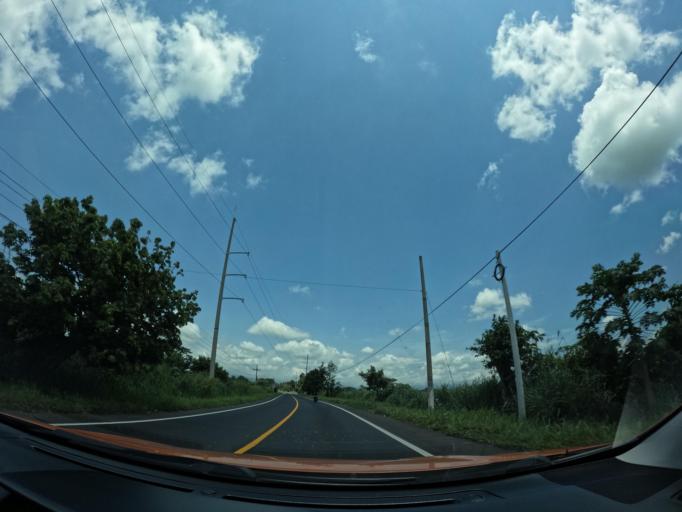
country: GT
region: Escuintla
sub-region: Municipio de Masagua
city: Masagua
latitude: 14.2454
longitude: -90.8109
